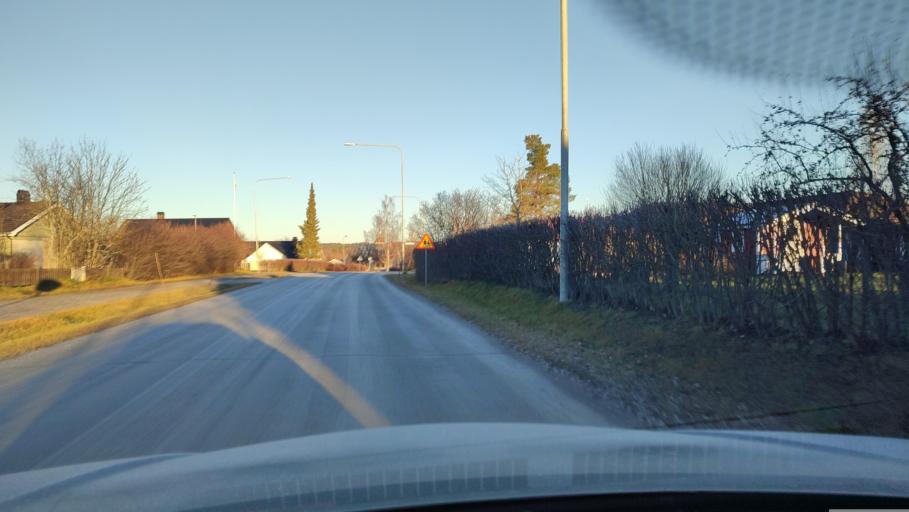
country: SE
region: Vaesterbotten
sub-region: Skelleftea Kommun
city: Viken
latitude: 64.7446
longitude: 20.9198
